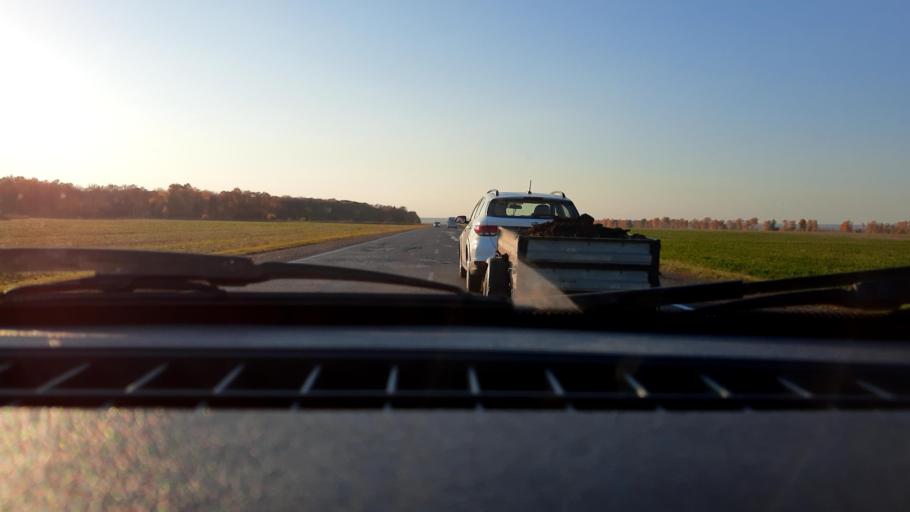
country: RU
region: Bashkortostan
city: Avdon
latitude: 54.8241
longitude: 55.6524
